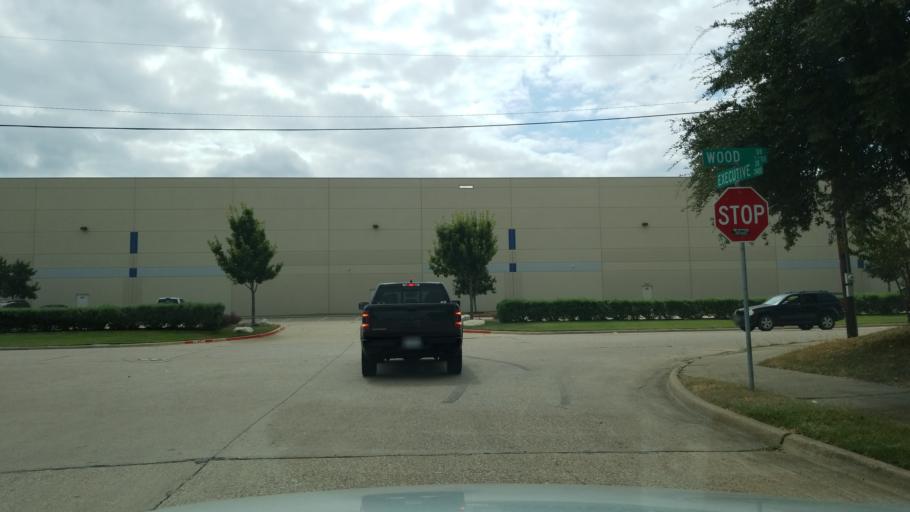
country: US
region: Texas
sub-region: Dallas County
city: Garland
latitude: 32.8870
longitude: -96.6815
